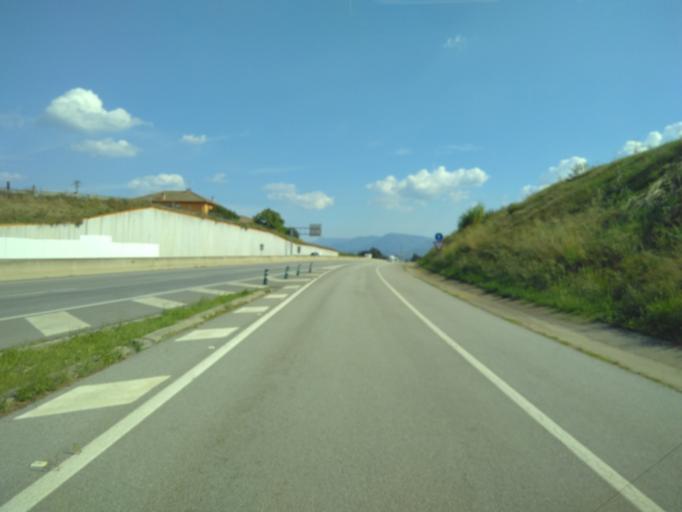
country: ES
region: Catalonia
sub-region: Provincia de Barcelona
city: Gurb
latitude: 41.9732
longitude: 2.2446
